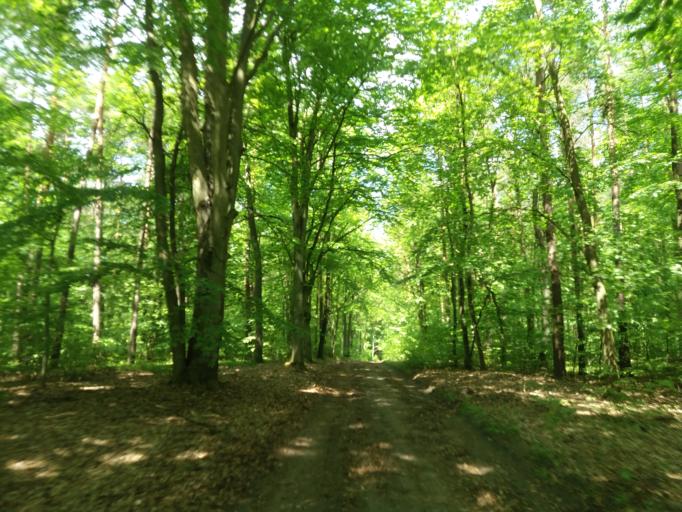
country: PL
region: West Pomeranian Voivodeship
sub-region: Powiat choszczenski
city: Bierzwnik
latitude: 53.0272
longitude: 15.6673
